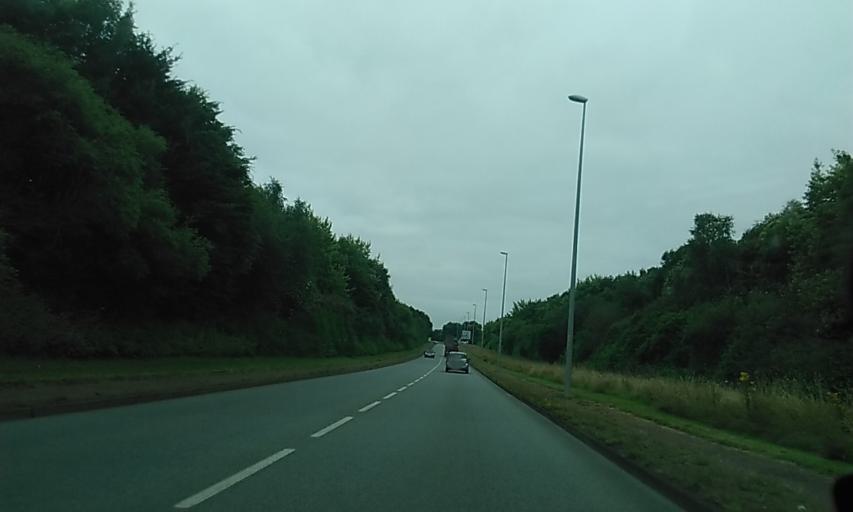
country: FR
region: Brittany
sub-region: Departement d'Ille-et-Vilaine
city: Cesson-Sevigne
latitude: 48.1194
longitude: -1.6207
